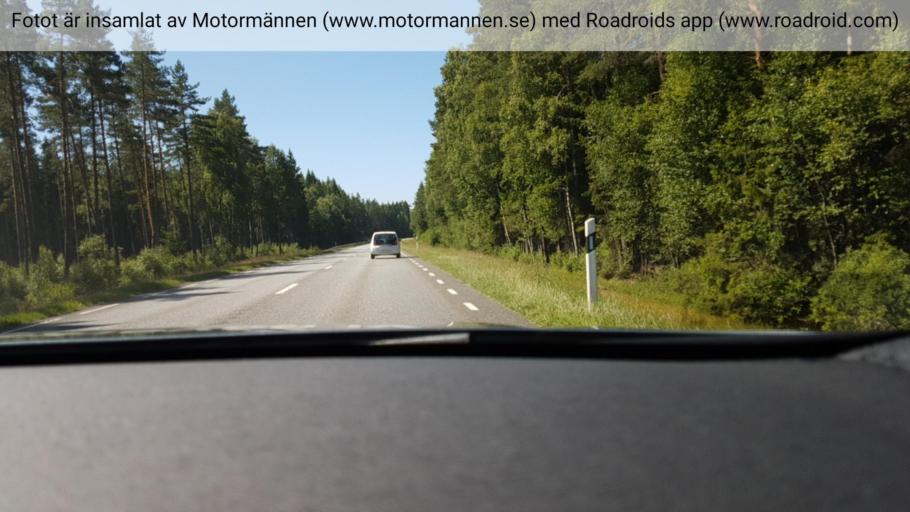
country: SE
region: Joenkoeping
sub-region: Gnosjo Kommun
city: Marieholm
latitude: 57.6415
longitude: 13.8008
